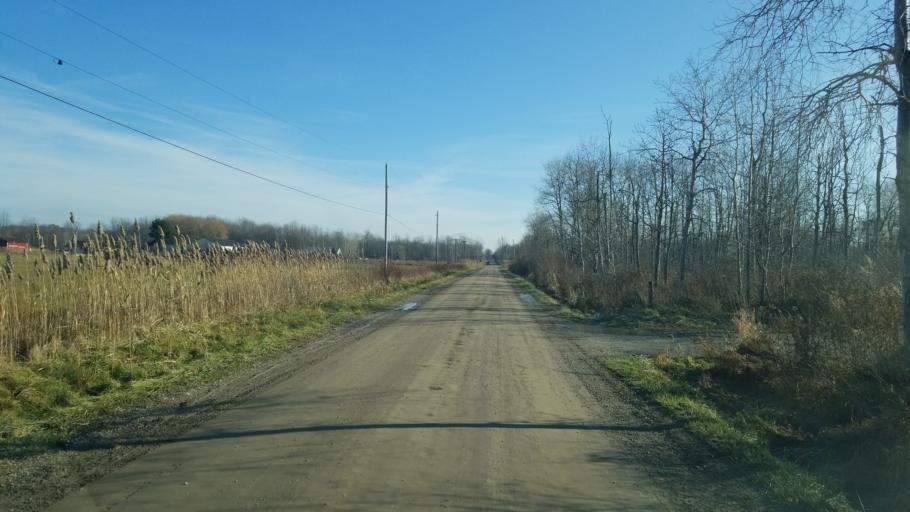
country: US
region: Ohio
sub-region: Ashtabula County
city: Jefferson
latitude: 41.7363
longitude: -80.6884
